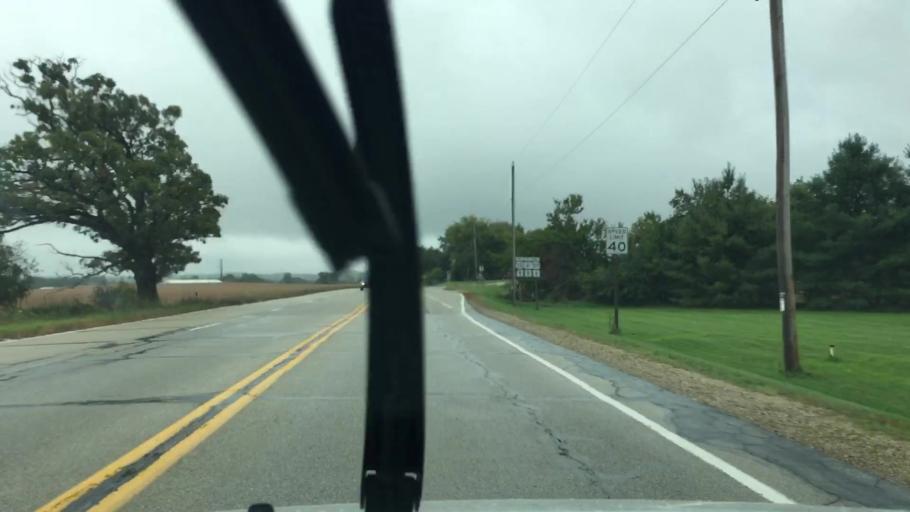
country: US
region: Wisconsin
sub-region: Walworth County
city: Whitewater
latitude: 42.8258
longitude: -88.7048
